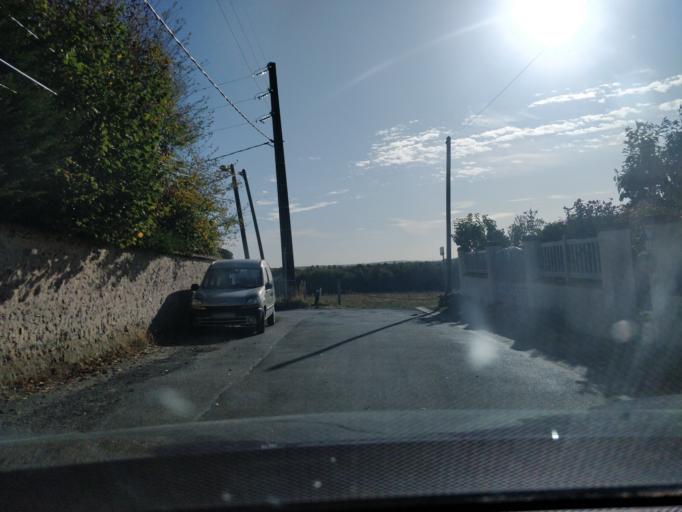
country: FR
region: Ile-de-France
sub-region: Departement de l'Essonne
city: Limours
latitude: 48.6241
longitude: 2.0743
